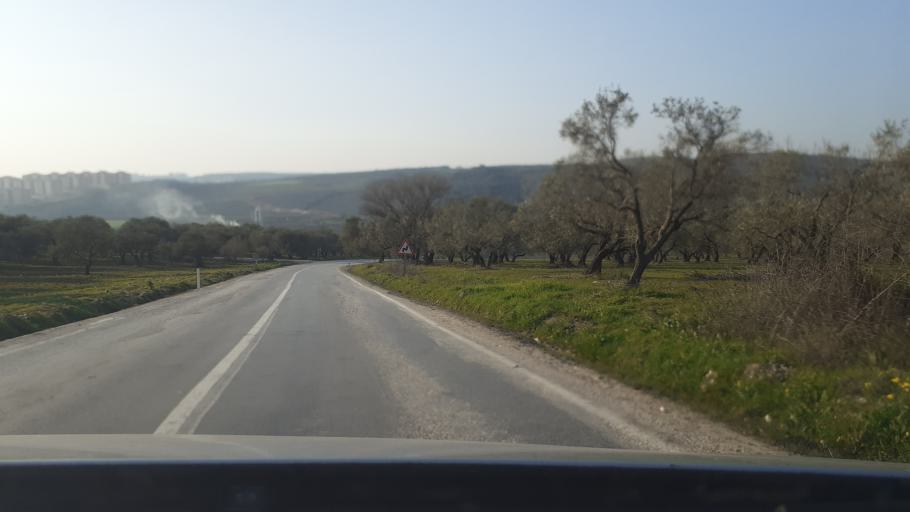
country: TR
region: Hatay
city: Oymakli
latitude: 36.1140
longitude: 36.2852
